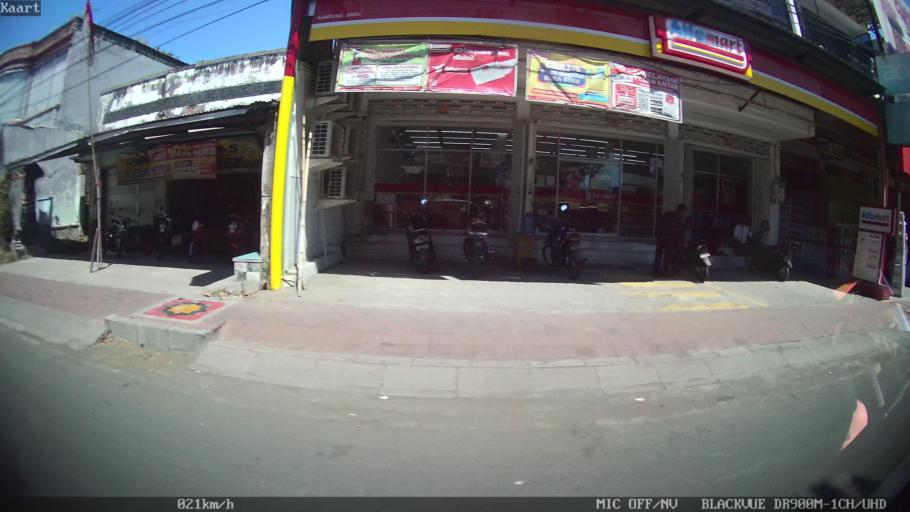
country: ID
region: Bali
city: Banjar Tambaksari
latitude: -8.1013
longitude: 115.0991
